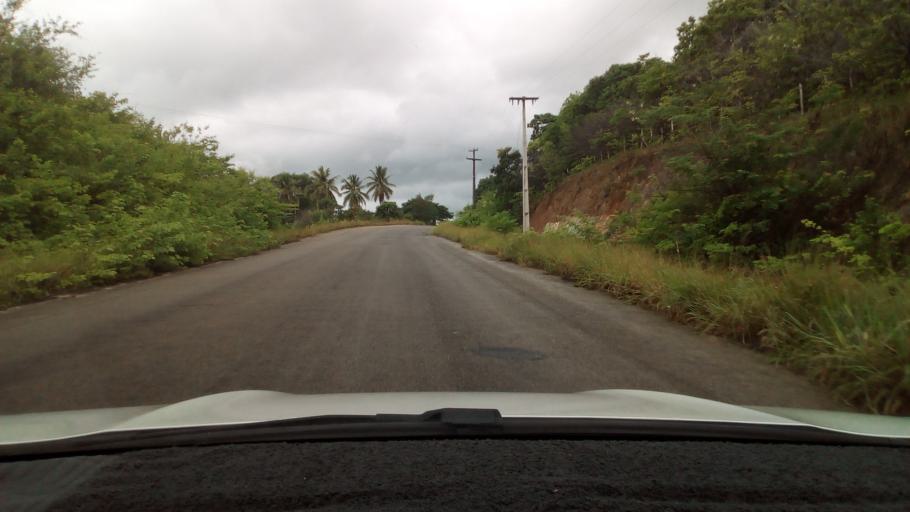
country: BR
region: Paraiba
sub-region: Pitimbu
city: Pitimbu
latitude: -7.3659
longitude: -34.8205
